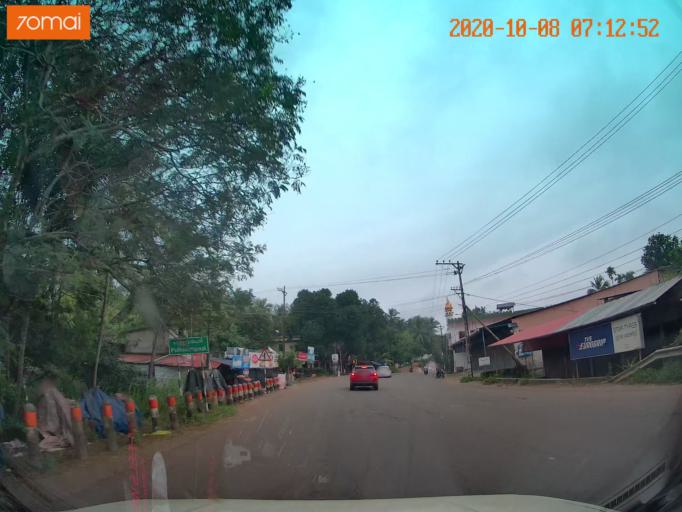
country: IN
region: Kerala
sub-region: Malappuram
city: Ponnani
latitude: 10.8078
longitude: 76.0078
